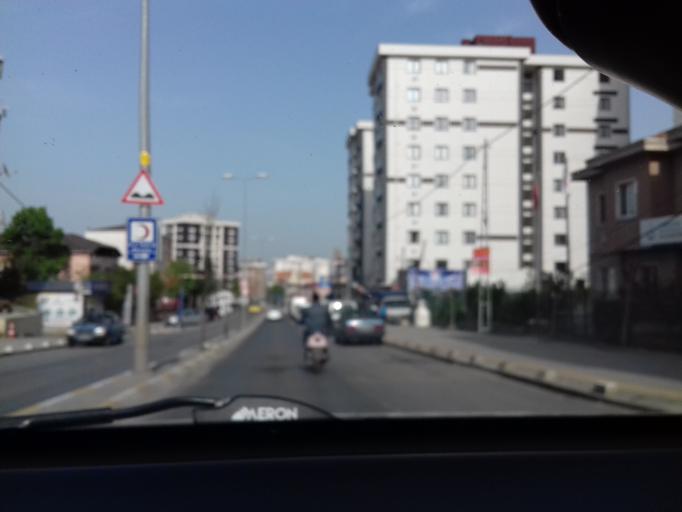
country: TR
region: Istanbul
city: Pendik
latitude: 40.9071
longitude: 29.2512
